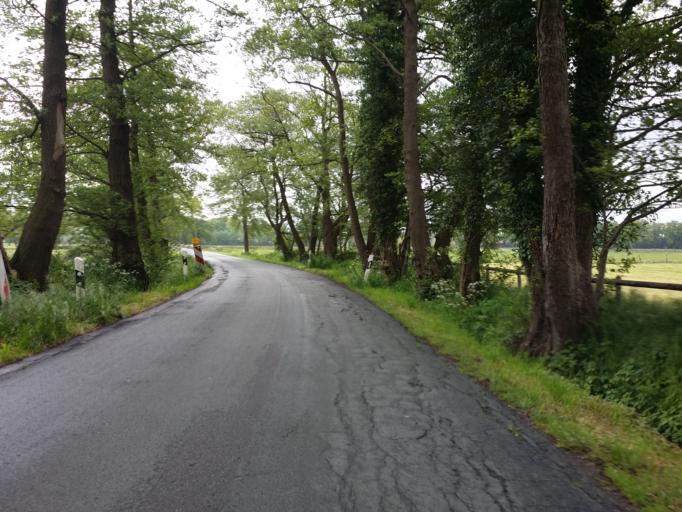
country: DE
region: Lower Saxony
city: Delmenhorst
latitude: 53.0283
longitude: 8.5862
